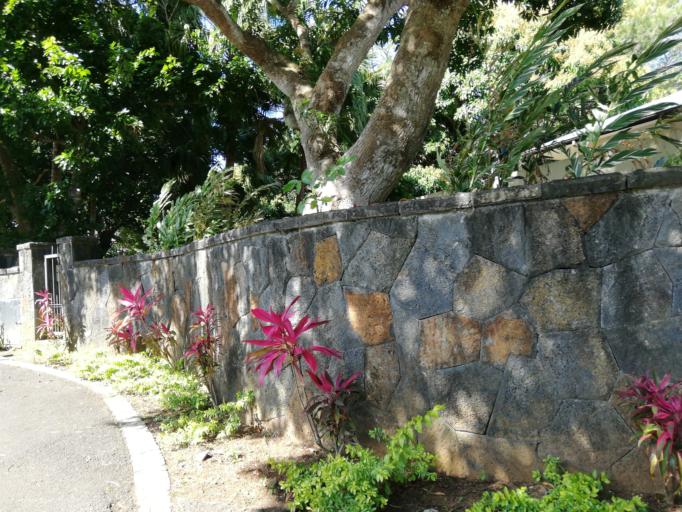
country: MU
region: Moka
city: Moka
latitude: -20.2180
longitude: 57.4940
